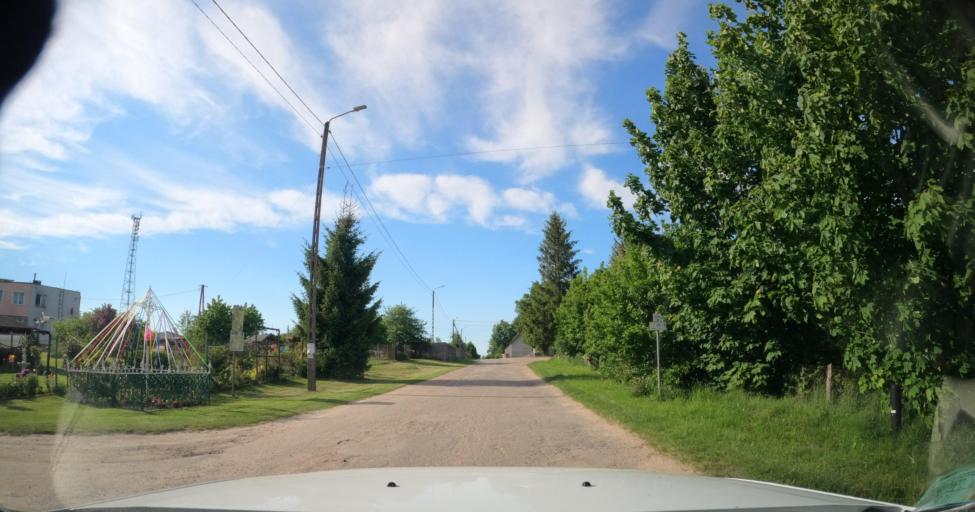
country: PL
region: Warmian-Masurian Voivodeship
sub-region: Powiat ostrodzki
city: Morag
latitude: 54.0633
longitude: 19.8895
